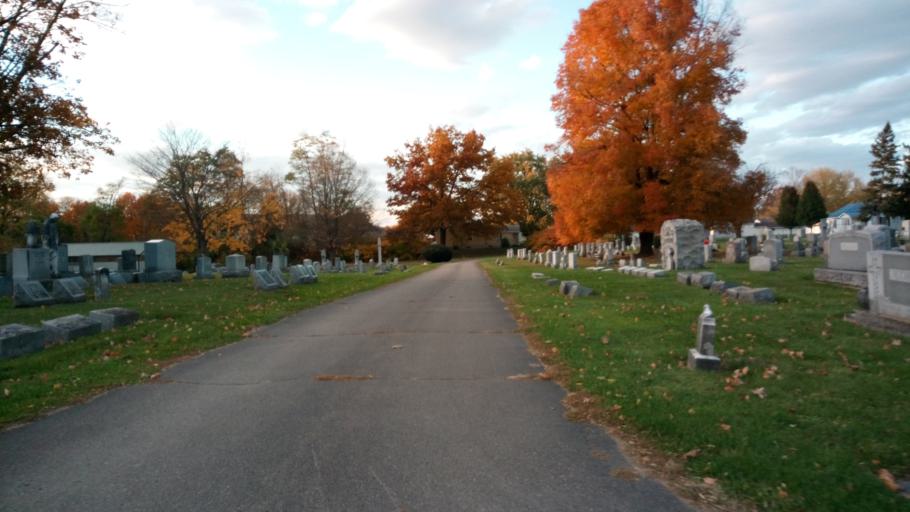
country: US
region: New York
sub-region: Chemung County
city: Southport
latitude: 42.0719
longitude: -76.8184
